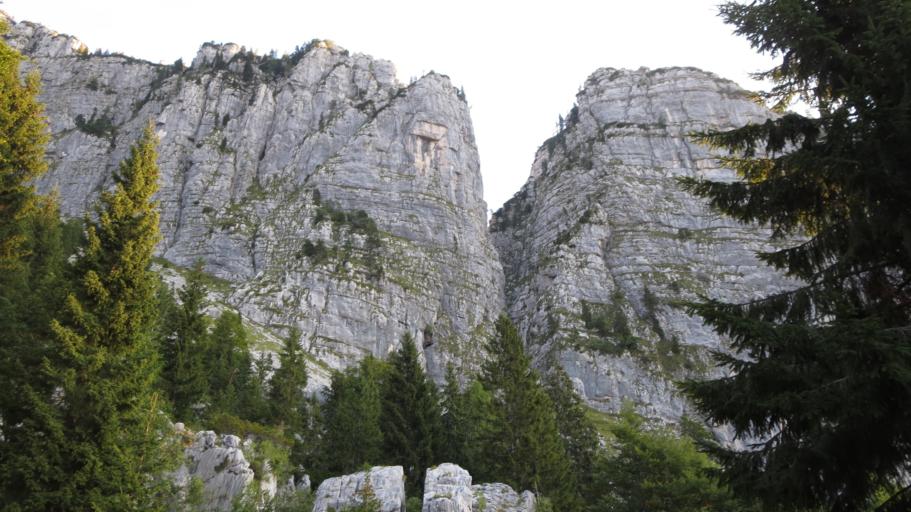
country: SI
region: Bovec
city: Bovec
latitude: 46.3396
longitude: 13.4864
